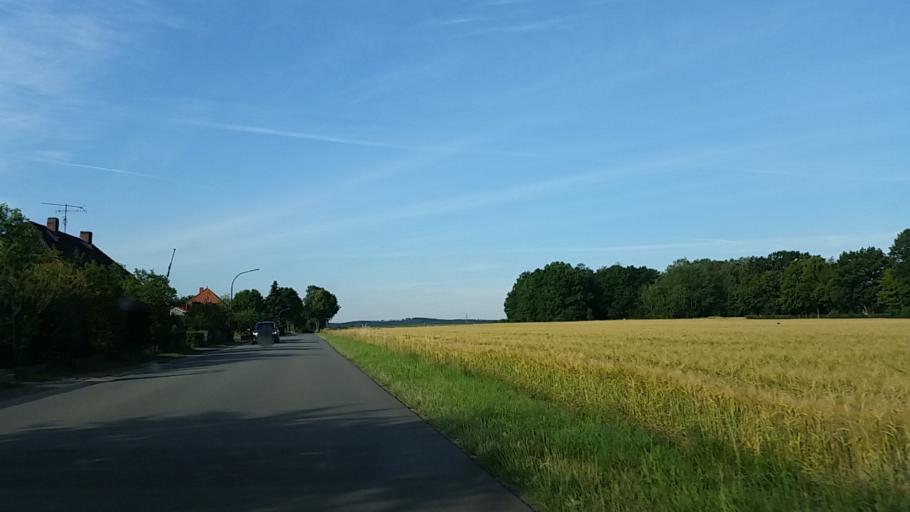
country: DE
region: Lower Saxony
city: Wieren
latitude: 52.9080
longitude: 10.6661
